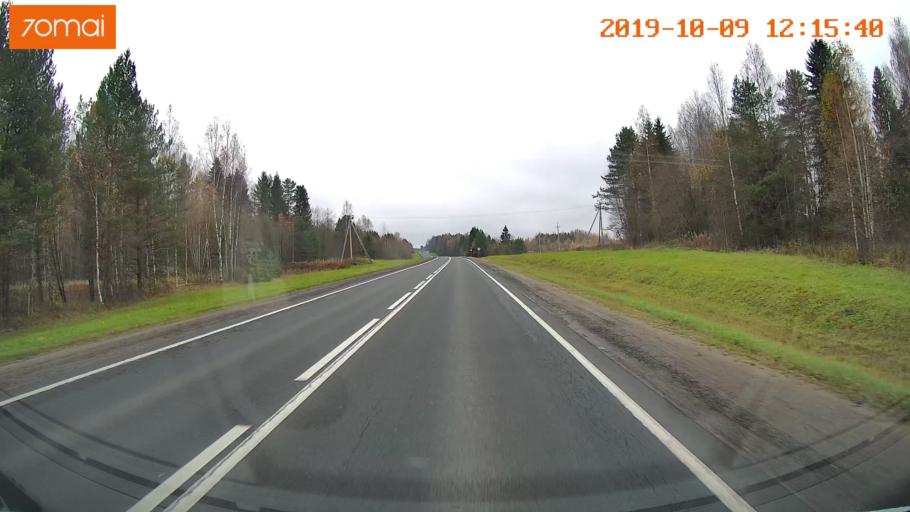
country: RU
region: Jaroslavl
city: Prechistoye
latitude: 58.4799
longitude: 40.3229
